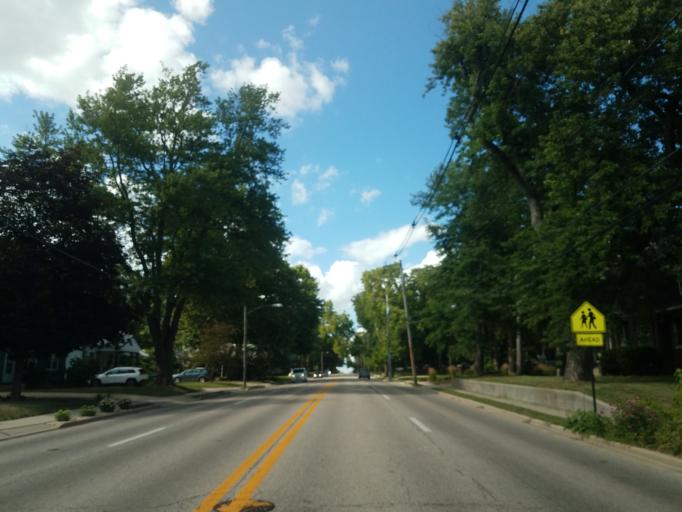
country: US
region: Illinois
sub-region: McLean County
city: Bloomington
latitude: 40.4971
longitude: -88.9821
